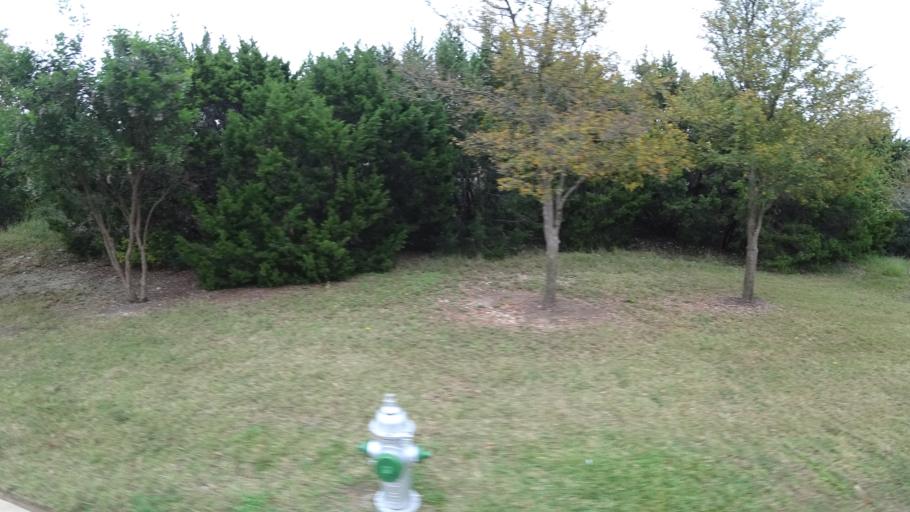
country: US
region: Texas
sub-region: Travis County
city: Bee Cave
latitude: 30.3587
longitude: -97.9093
